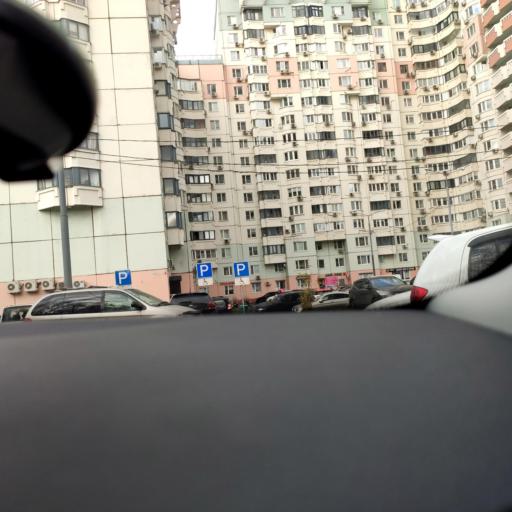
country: RU
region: Moskovskaya
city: Kozhukhovo
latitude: 55.6821
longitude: 37.6448
